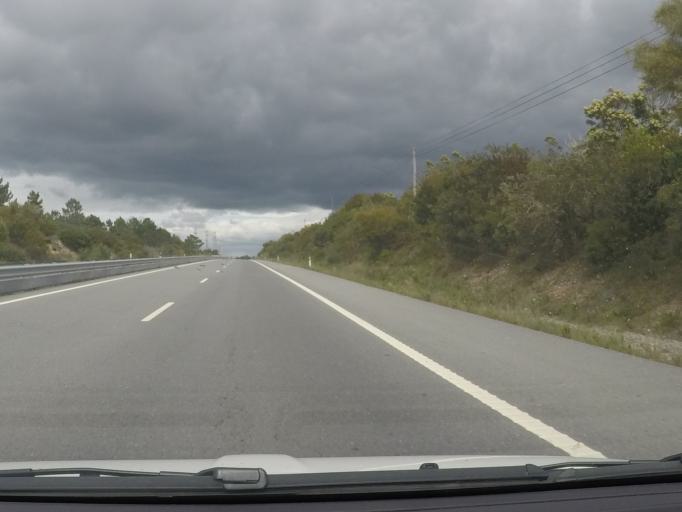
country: PT
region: Setubal
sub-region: Santiago do Cacem
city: Santo Andre
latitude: 37.9908
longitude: -8.7694
